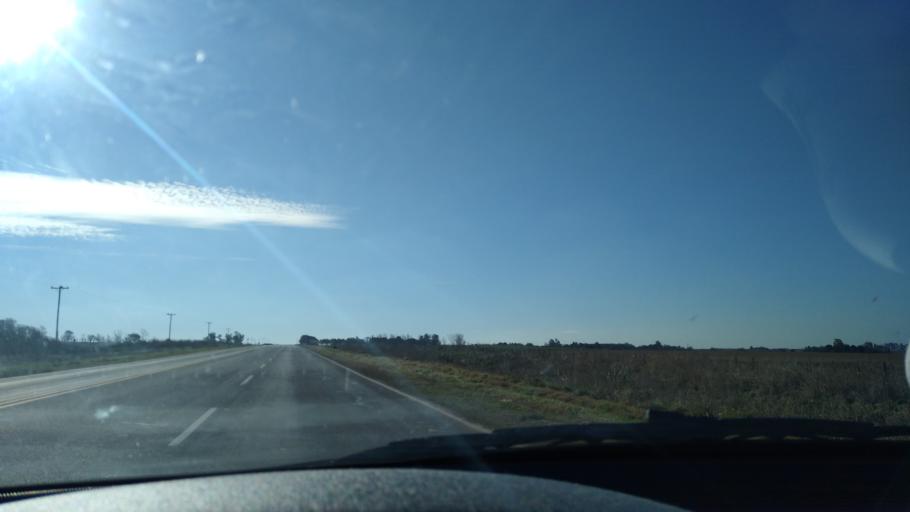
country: AR
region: Entre Rios
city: Aranguren
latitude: -32.4004
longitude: -60.3264
